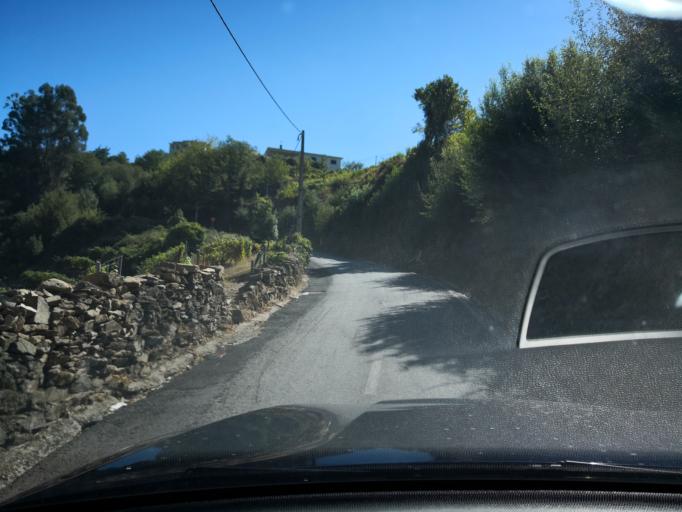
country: PT
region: Vila Real
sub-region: Santa Marta de Penaguiao
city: Santa Marta de Penaguiao
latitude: 41.2482
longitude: -7.8132
